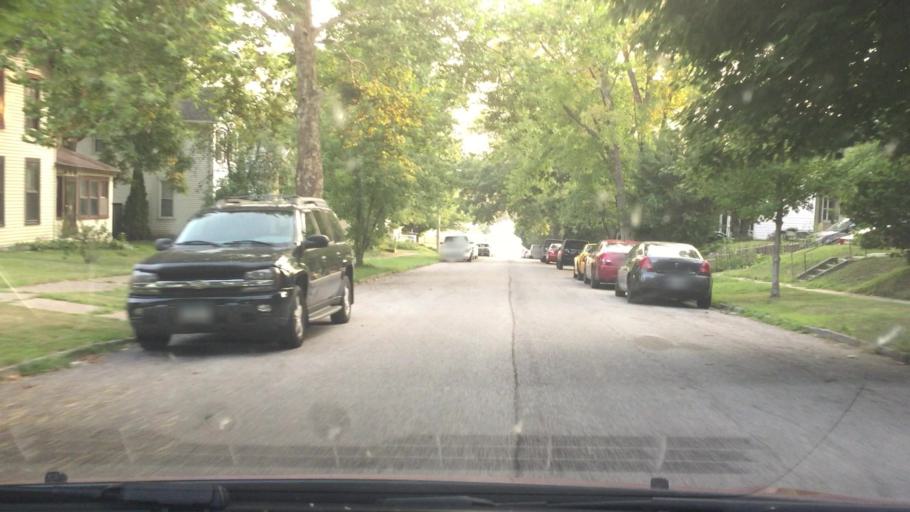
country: US
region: Iowa
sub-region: Muscatine County
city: Muscatine
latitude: 41.4303
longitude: -91.0451
